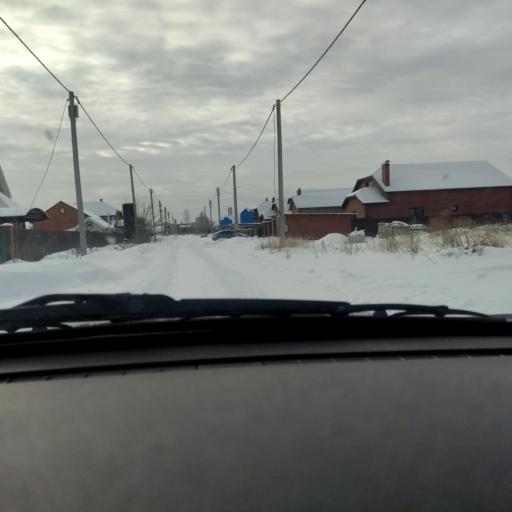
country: RU
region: Samara
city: Tol'yatti
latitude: 53.5599
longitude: 49.3757
